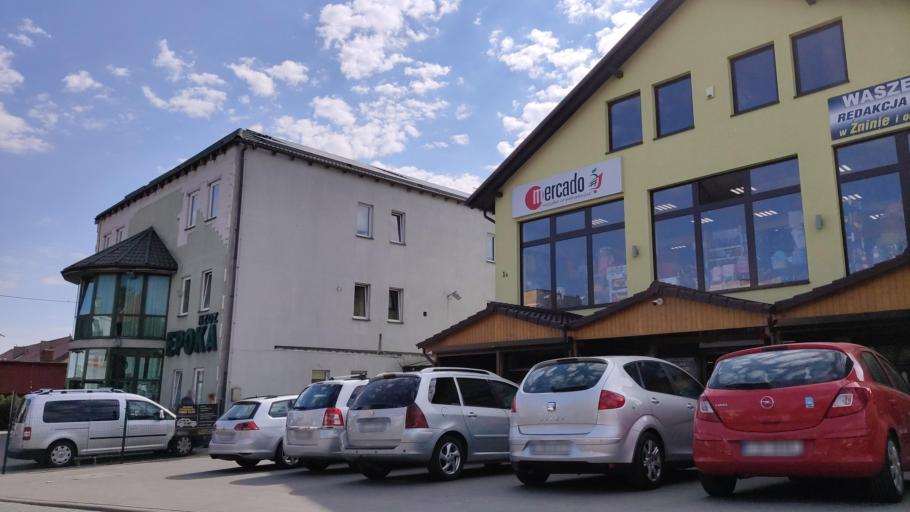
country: PL
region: Kujawsko-Pomorskie
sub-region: Powiat zninski
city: Znin
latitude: 52.8494
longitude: 17.7173
